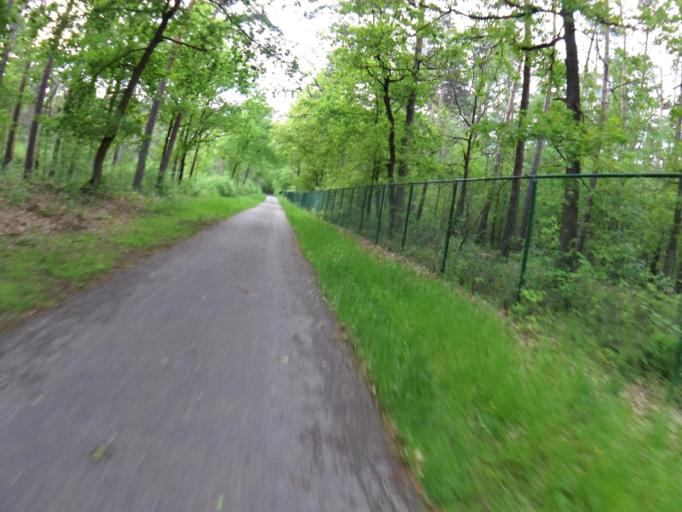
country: BE
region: Flanders
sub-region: Provincie Limburg
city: Genk
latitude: 50.9523
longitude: 5.5316
